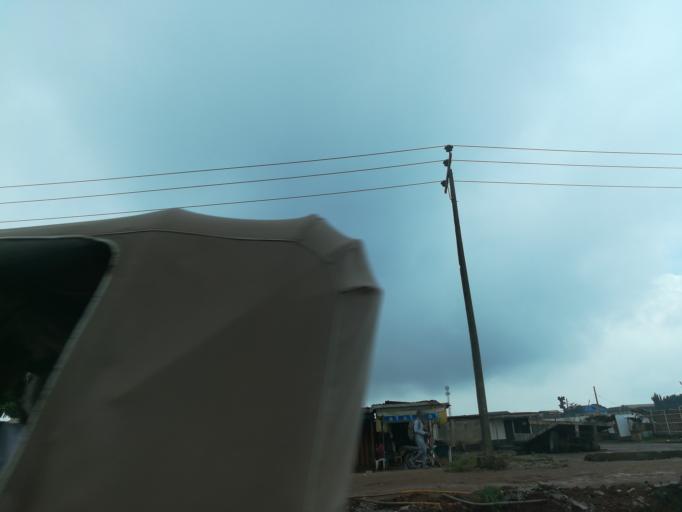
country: NG
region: Lagos
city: Ikorodu
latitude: 6.6506
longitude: 3.5187
